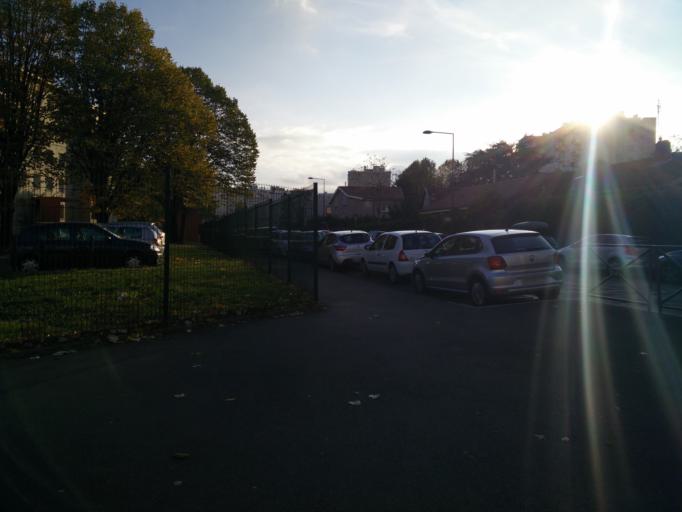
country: FR
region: Rhone-Alpes
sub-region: Departement du Rhone
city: Villeurbanne
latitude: 45.7600
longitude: 4.8809
